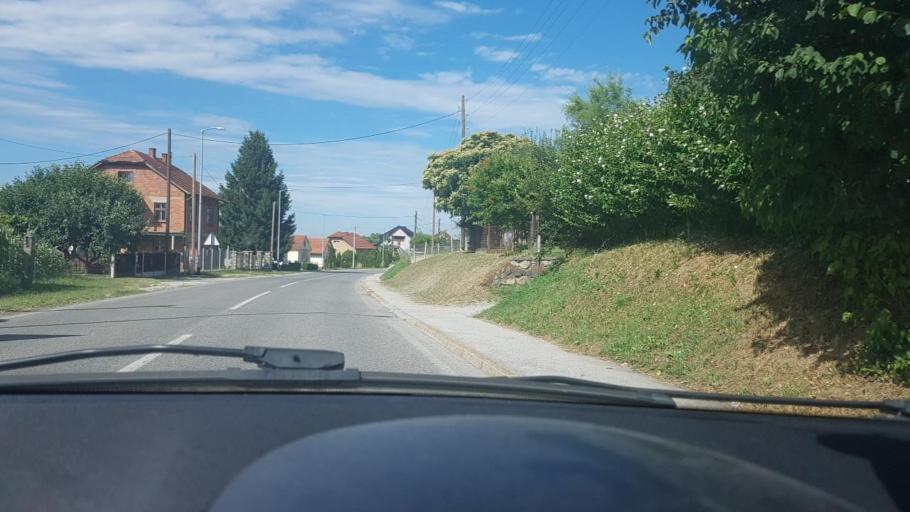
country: HR
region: Varazdinska
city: Lepoglava
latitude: 46.2094
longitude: 16.0556
